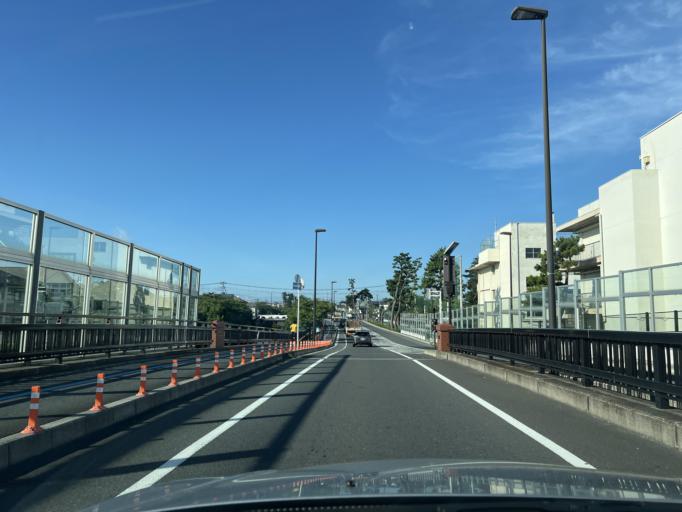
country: JP
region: Chiba
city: Funabashi
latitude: 35.7271
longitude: 139.9383
